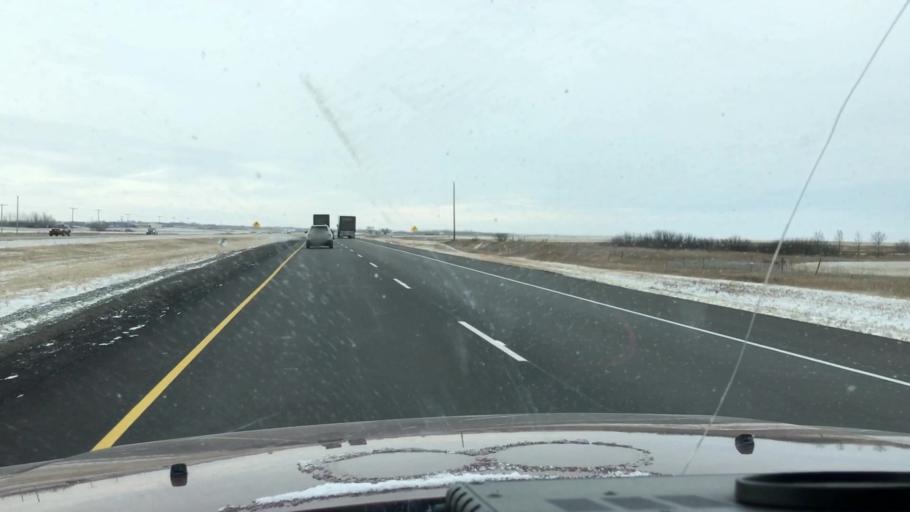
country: CA
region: Saskatchewan
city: Saskatoon
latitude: 51.7857
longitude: -106.4804
